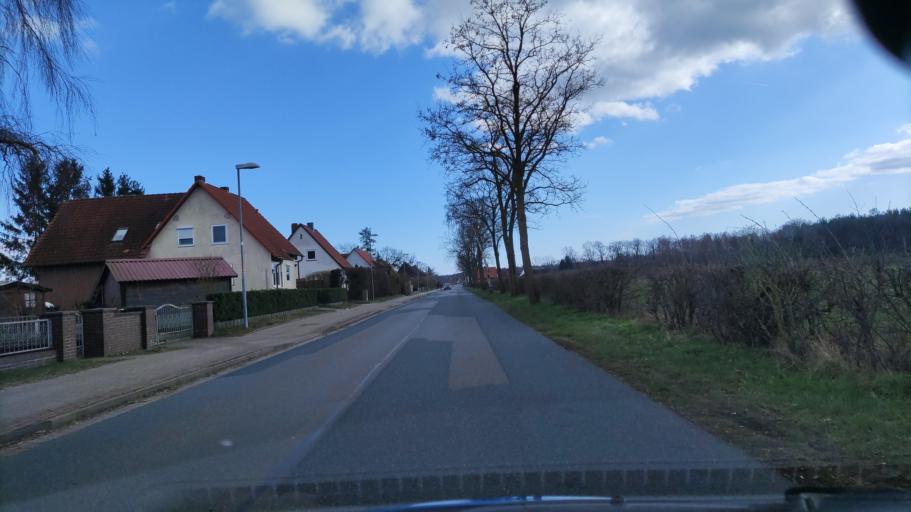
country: DE
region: Lower Saxony
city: Beedenbostel
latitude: 52.6384
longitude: 10.2108
